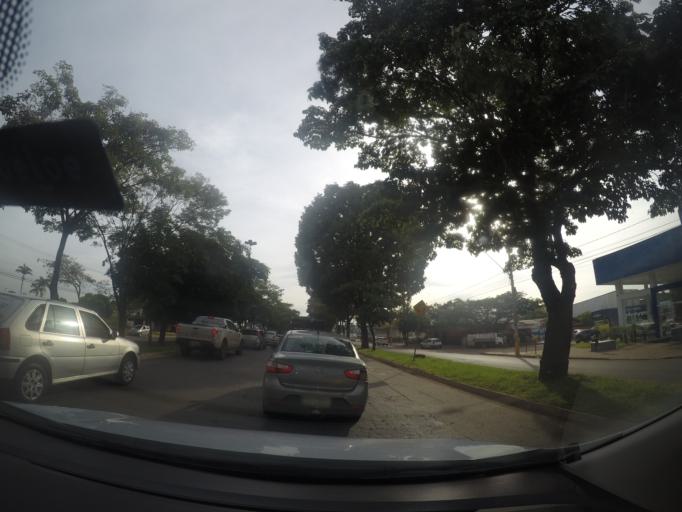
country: BR
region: Goias
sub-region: Goiania
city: Goiania
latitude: -16.6979
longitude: -49.3294
